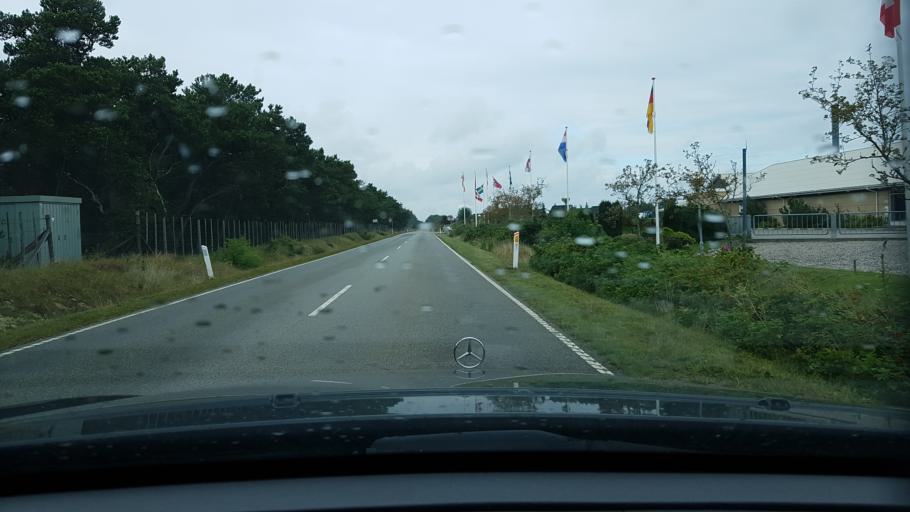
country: DK
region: North Denmark
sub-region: Alborg Kommune
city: Hals
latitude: 56.8246
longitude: 10.2690
